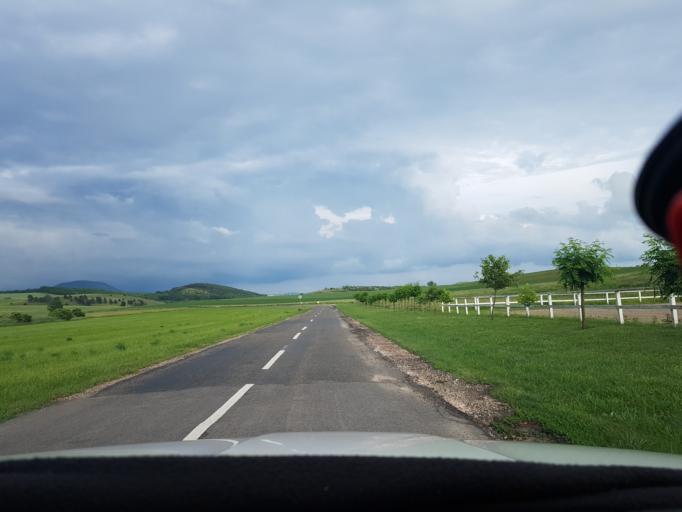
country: HU
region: Komarom-Esztergom
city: Bajna
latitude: 47.7086
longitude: 18.5912
